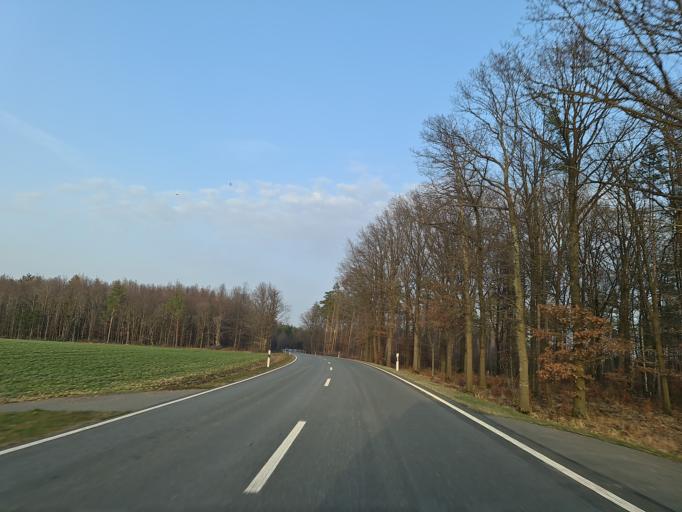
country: DE
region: Thuringia
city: Tautenhain
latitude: 50.9209
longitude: 11.9373
